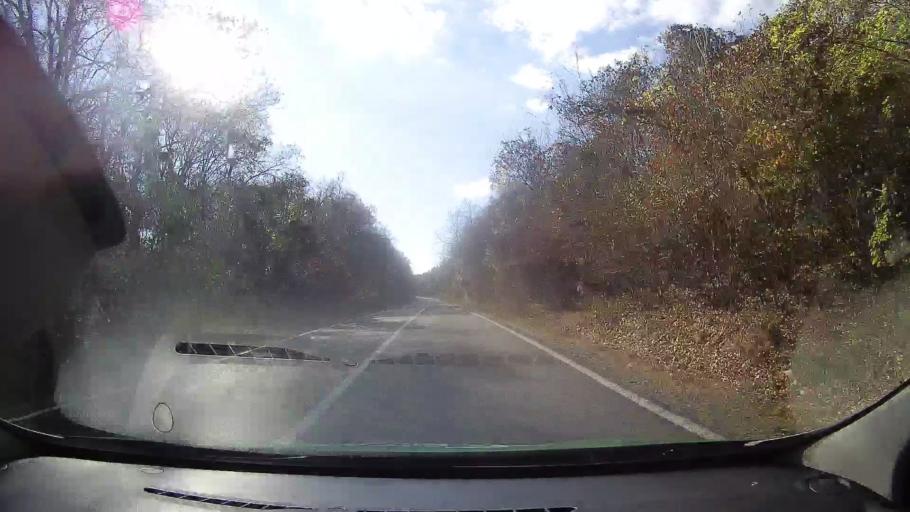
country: RO
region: Tulcea
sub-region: Oras Babadag
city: Babadag
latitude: 44.8414
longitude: 28.6971
